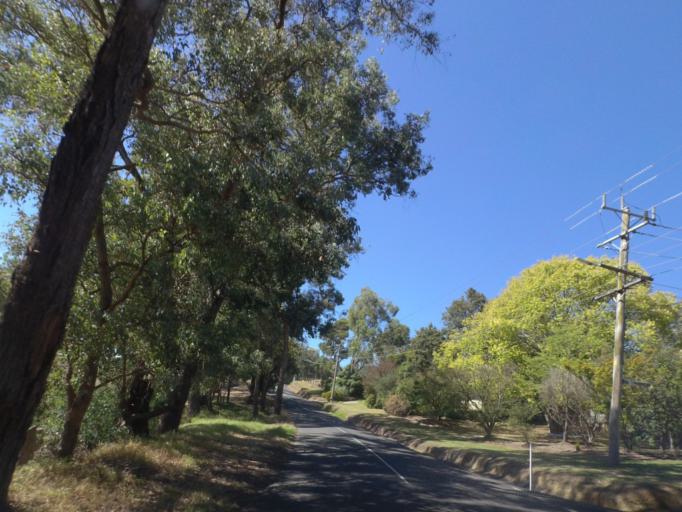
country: AU
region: Victoria
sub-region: Maroondah
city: Croydon Hills
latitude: -37.7513
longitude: 145.2663
